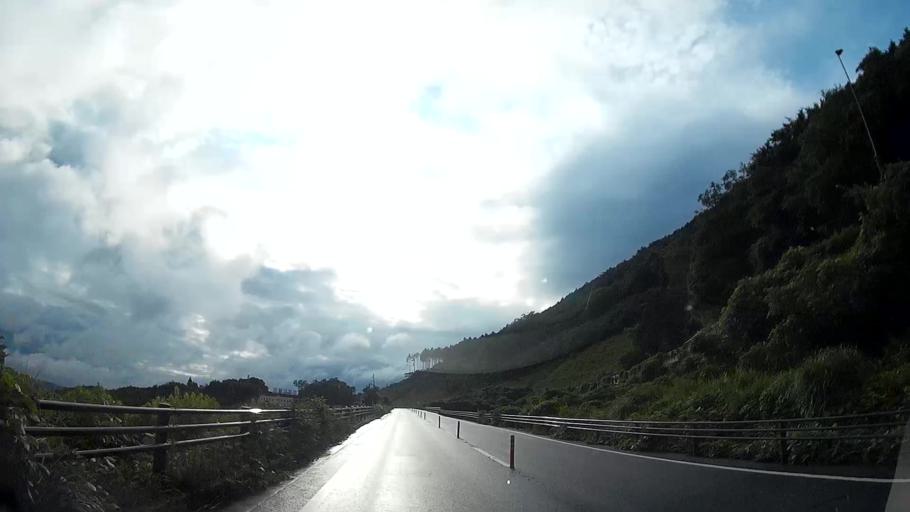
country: JP
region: Kumamoto
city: Ozu
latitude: 32.8763
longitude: 130.9453
